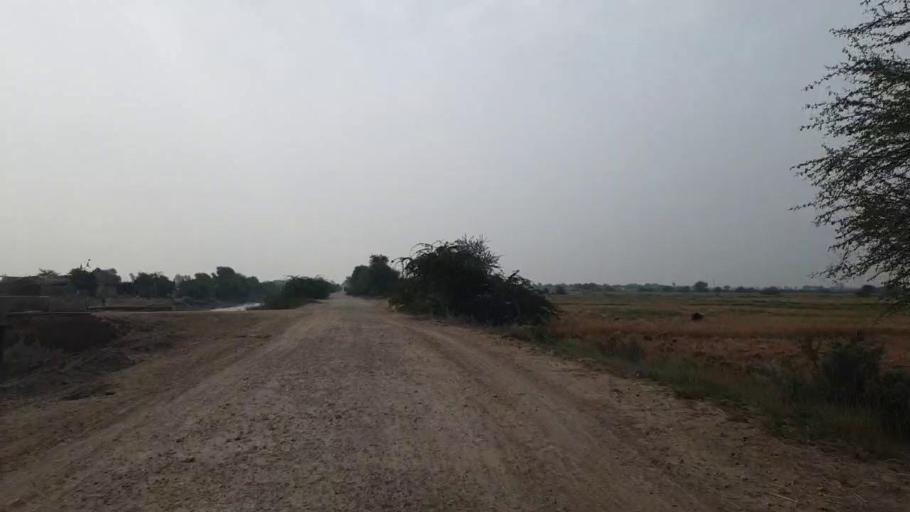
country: PK
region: Sindh
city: Kario
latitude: 24.8876
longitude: 68.5260
